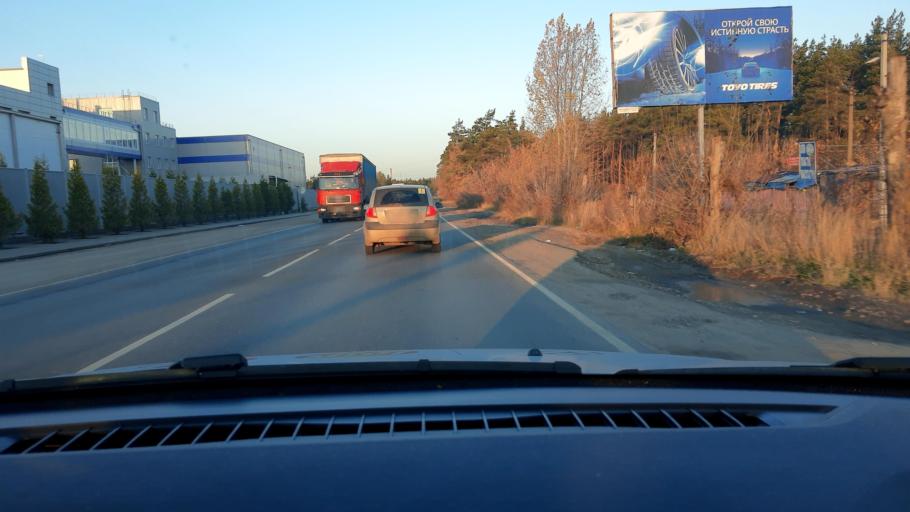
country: RU
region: Nizjnij Novgorod
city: Dzerzhinsk
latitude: 56.2580
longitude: 43.4663
